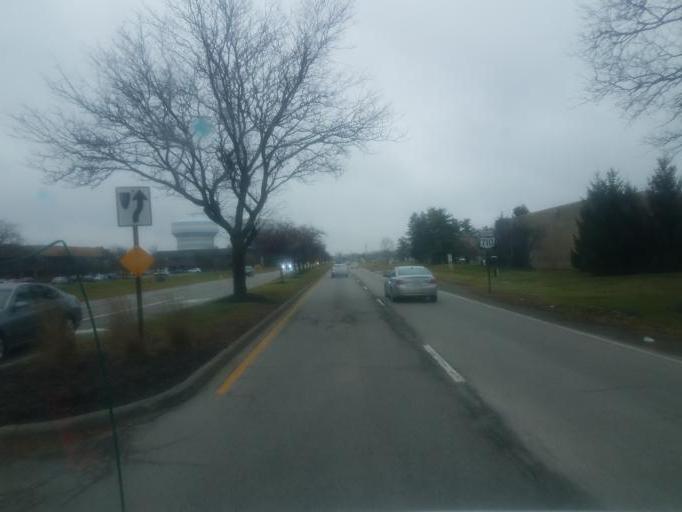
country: US
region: Ohio
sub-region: Franklin County
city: Worthington
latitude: 40.0999
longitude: -82.9935
